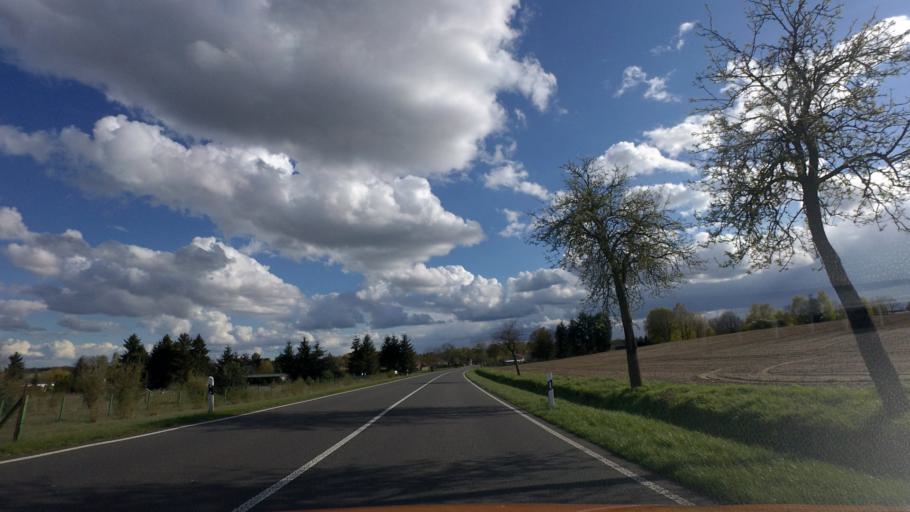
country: DE
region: Brandenburg
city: Gumtow
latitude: 53.0627
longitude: 12.2336
